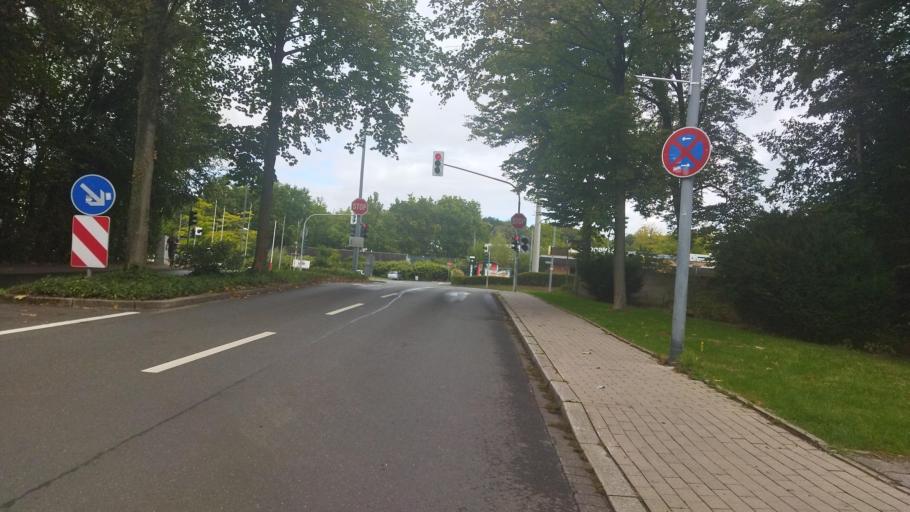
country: DE
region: North Rhine-Westphalia
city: Herten
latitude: 51.5938
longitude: 7.1275
